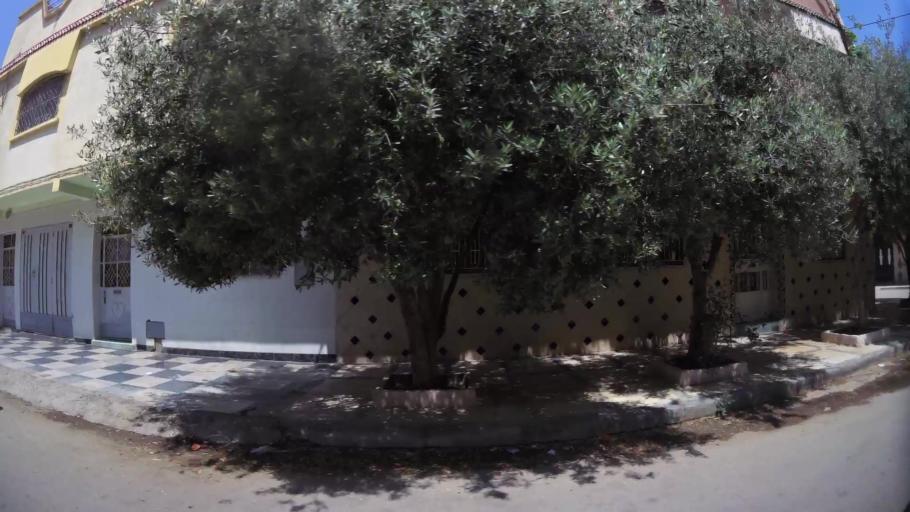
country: MA
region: Oriental
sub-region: Oujda-Angad
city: Oujda
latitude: 34.6903
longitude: -1.8880
